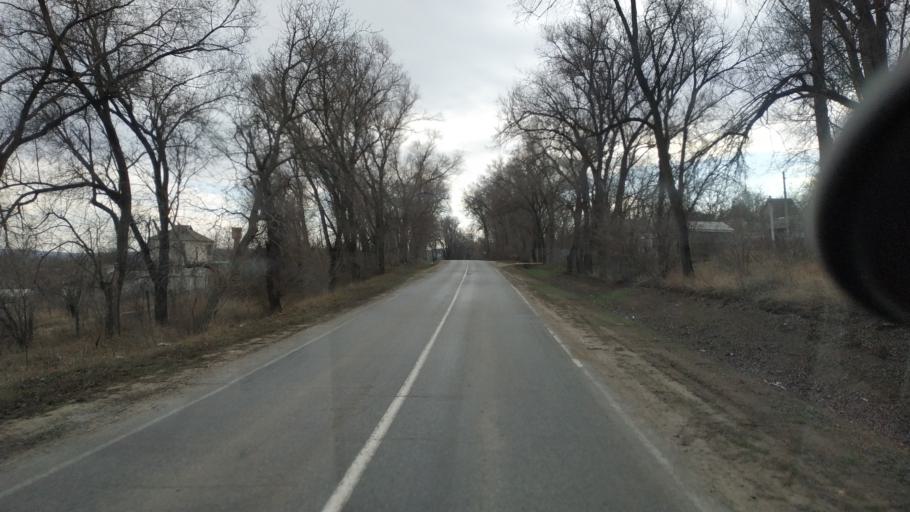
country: MD
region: Chisinau
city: Vadul lui Voda
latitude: 47.1235
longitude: 29.0638
